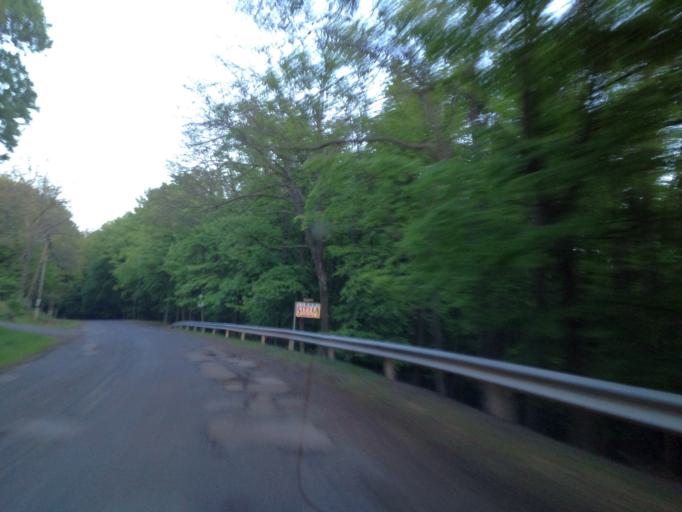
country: HU
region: Heves
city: Gyongyostarjan
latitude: 47.8935
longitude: 19.8704
